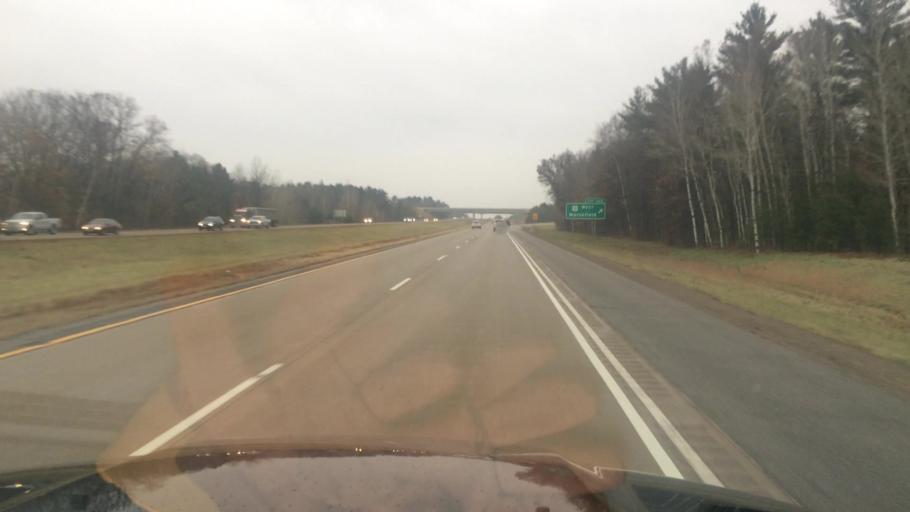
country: US
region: Wisconsin
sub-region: Portage County
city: Stevens Point
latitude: 44.6033
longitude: -89.6188
